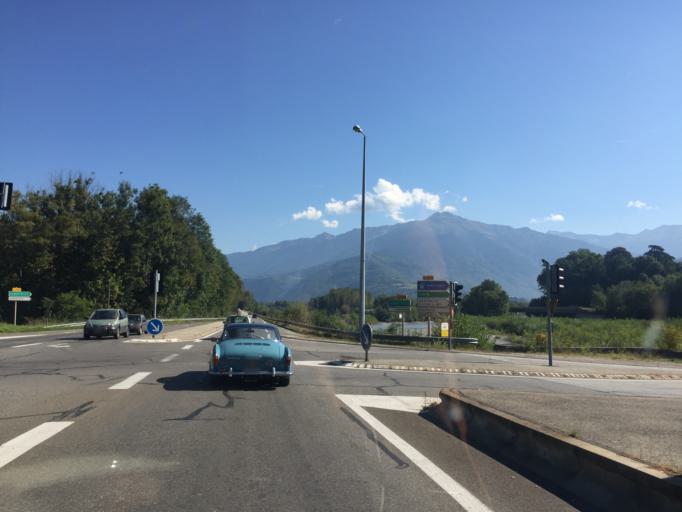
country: FR
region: Rhone-Alpes
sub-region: Departement de la Savoie
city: Aiton
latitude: 45.5627
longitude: 6.1980
